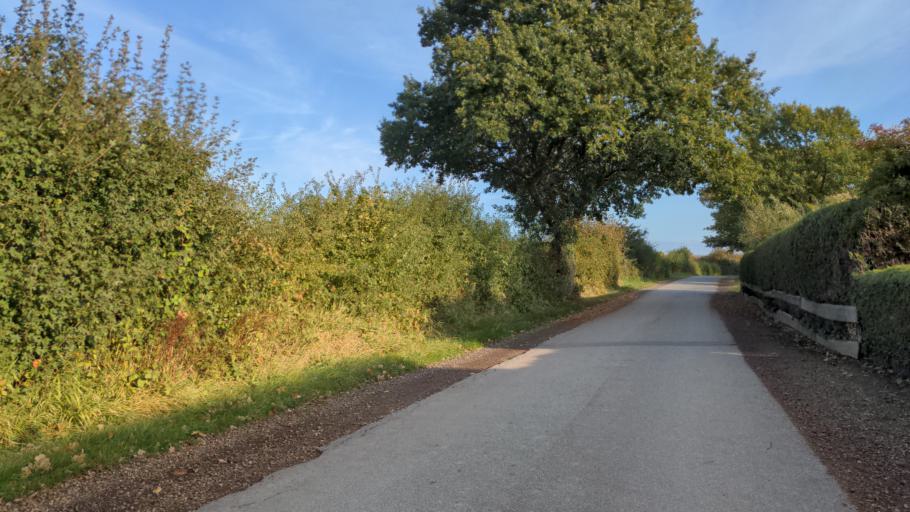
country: DE
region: Schleswig-Holstein
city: Manhagen
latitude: 54.1857
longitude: 10.9458
